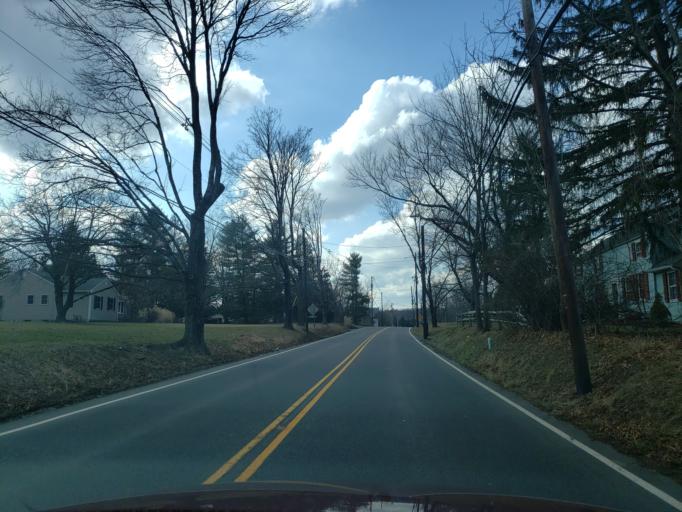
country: US
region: New Jersey
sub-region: Hunterdon County
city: Flemington
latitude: 40.4985
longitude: -74.8785
